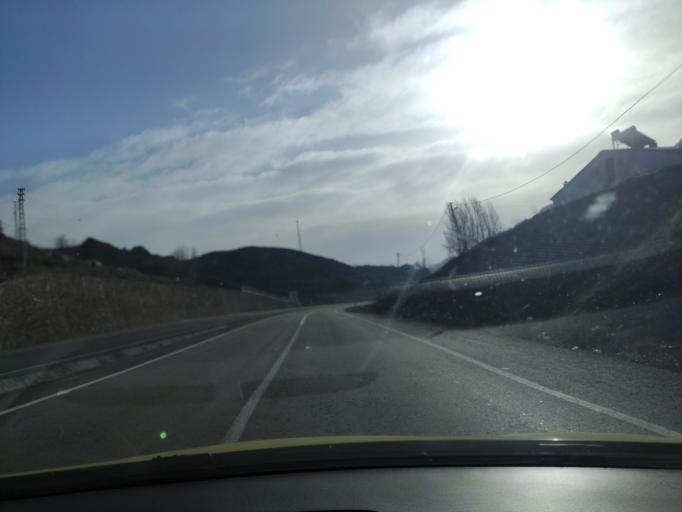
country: TR
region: Gumushane
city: Kale
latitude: 40.4049
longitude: 39.6170
